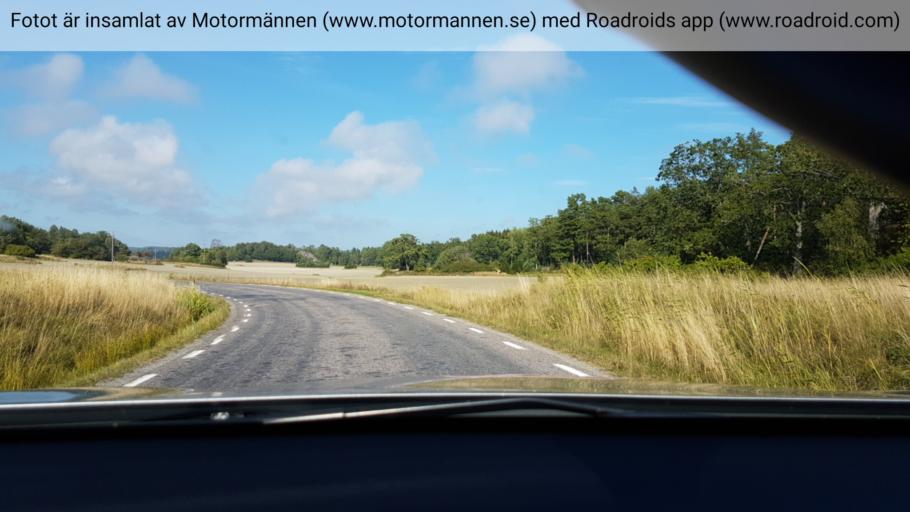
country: SE
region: Stockholm
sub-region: Nynashamns Kommun
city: Osmo
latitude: 58.8891
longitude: 17.7926
